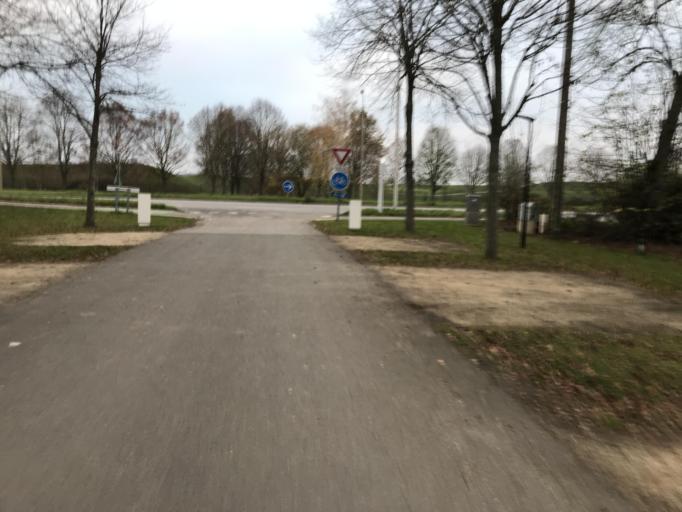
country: FR
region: Ile-de-France
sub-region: Departement des Yvelines
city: Magny-les-Hameaux
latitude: 48.7483
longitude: 2.0725
